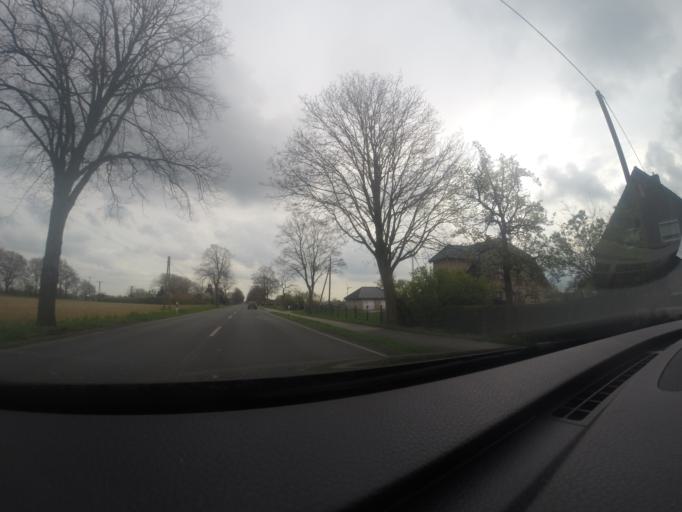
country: DE
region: North Rhine-Westphalia
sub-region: Regierungsbezirk Dusseldorf
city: Alpen
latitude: 51.5850
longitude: 6.5489
